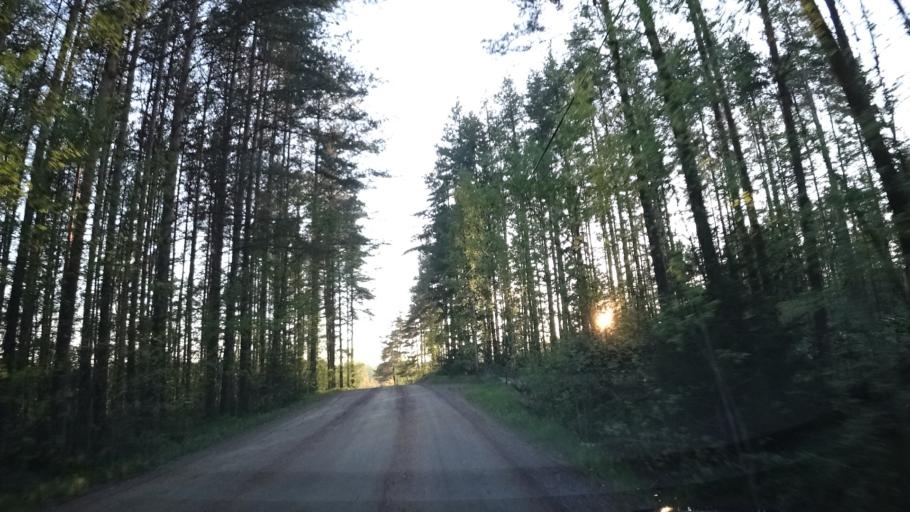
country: FI
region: Uusimaa
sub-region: Helsinki
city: Siuntio
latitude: 60.0646
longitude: 24.2209
